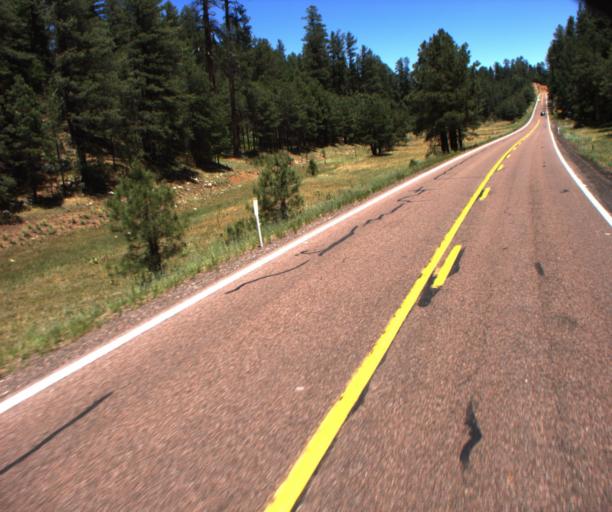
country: US
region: Arizona
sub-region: Gila County
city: Pine
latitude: 34.5015
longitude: -111.3660
